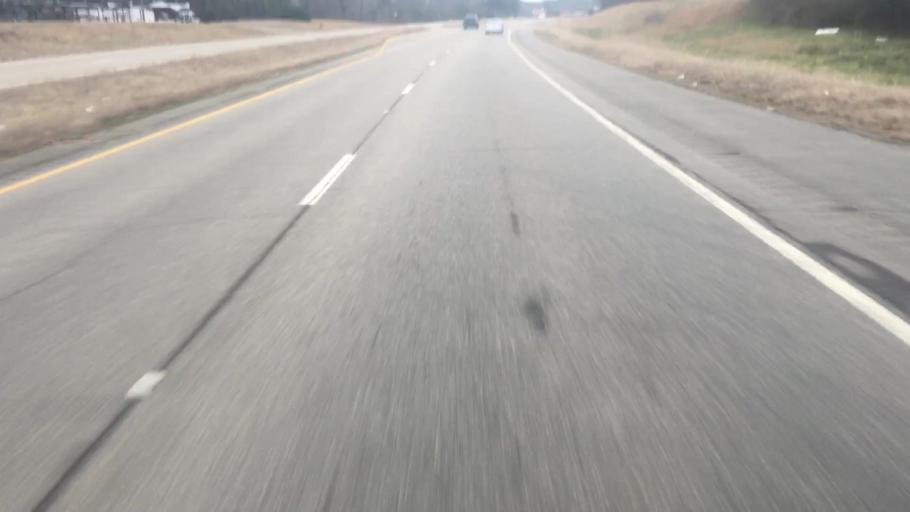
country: US
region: Alabama
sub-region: Walker County
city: Cordova
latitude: 33.8214
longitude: -87.1597
